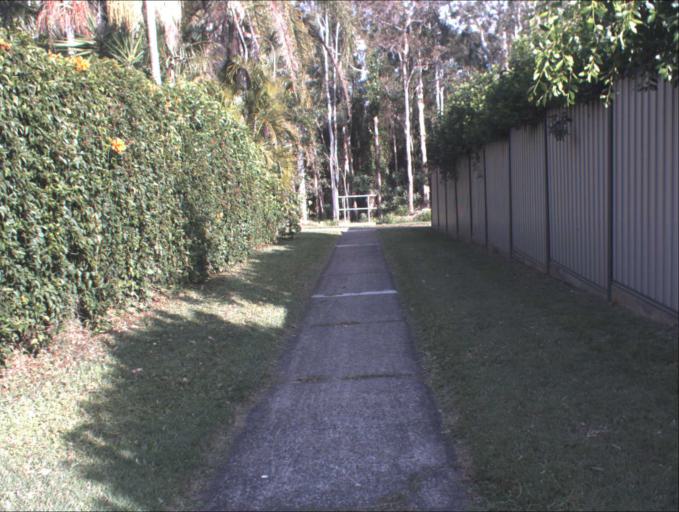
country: AU
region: Queensland
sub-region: Logan
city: Park Ridge South
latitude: -27.6797
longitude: 153.0350
